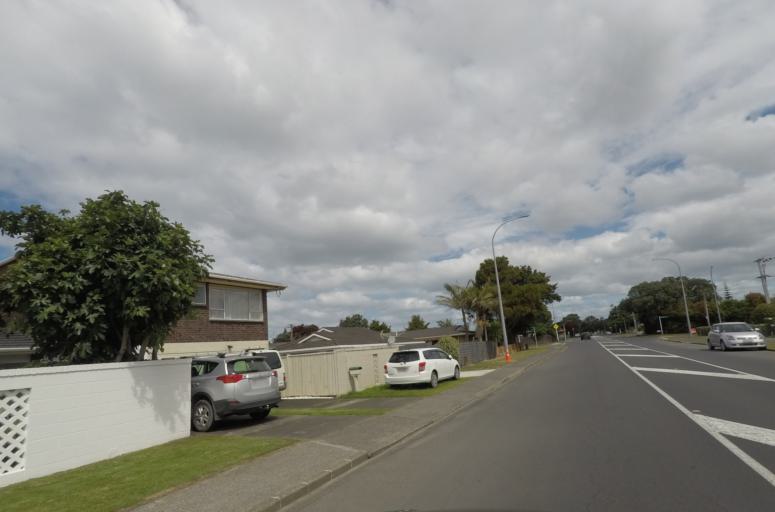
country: NZ
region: Auckland
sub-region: Auckland
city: Rothesay Bay
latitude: -36.5886
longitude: 174.6929
